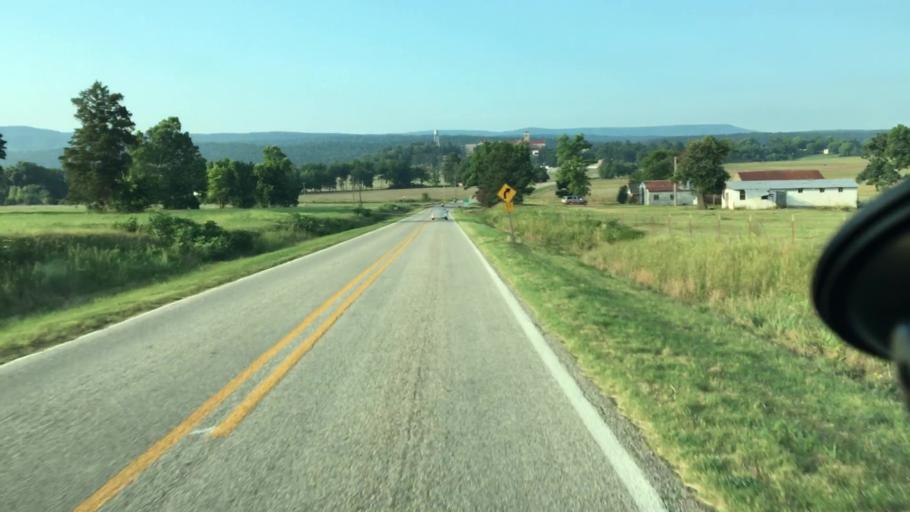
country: US
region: Arkansas
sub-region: Logan County
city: Paris
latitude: 35.3105
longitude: -93.6326
